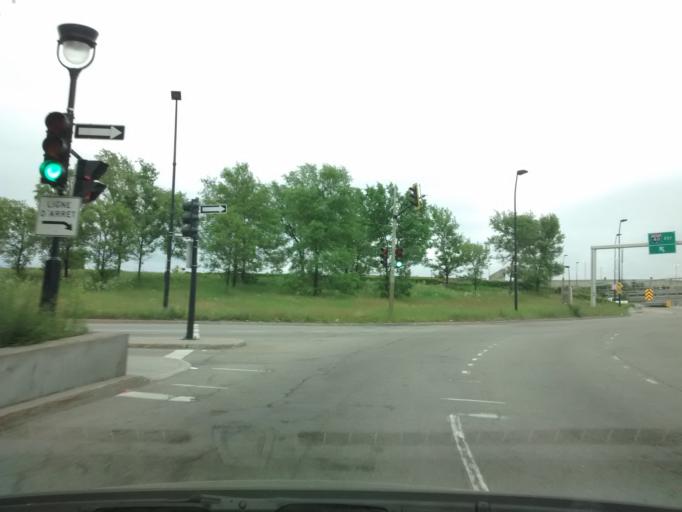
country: CA
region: Quebec
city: Mont-Royal
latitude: 45.5312
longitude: -73.6500
